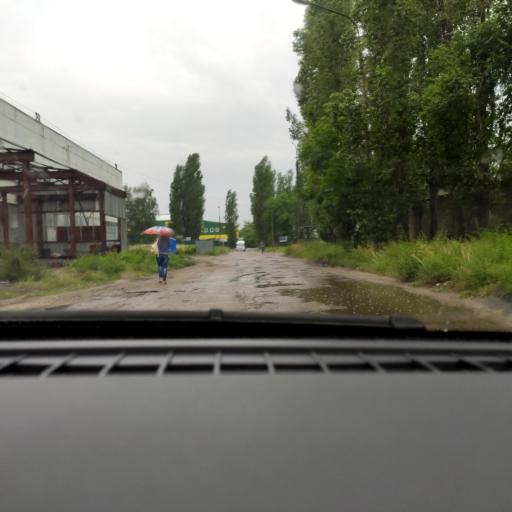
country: RU
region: Voronezj
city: Somovo
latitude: 51.7160
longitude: 39.2880
